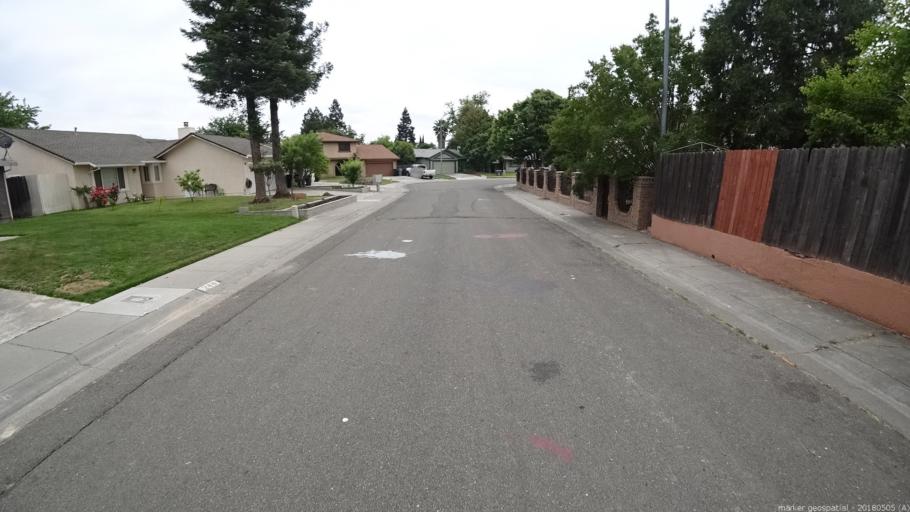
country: US
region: California
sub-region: Sacramento County
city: Rio Linda
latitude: 38.6540
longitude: -121.4643
